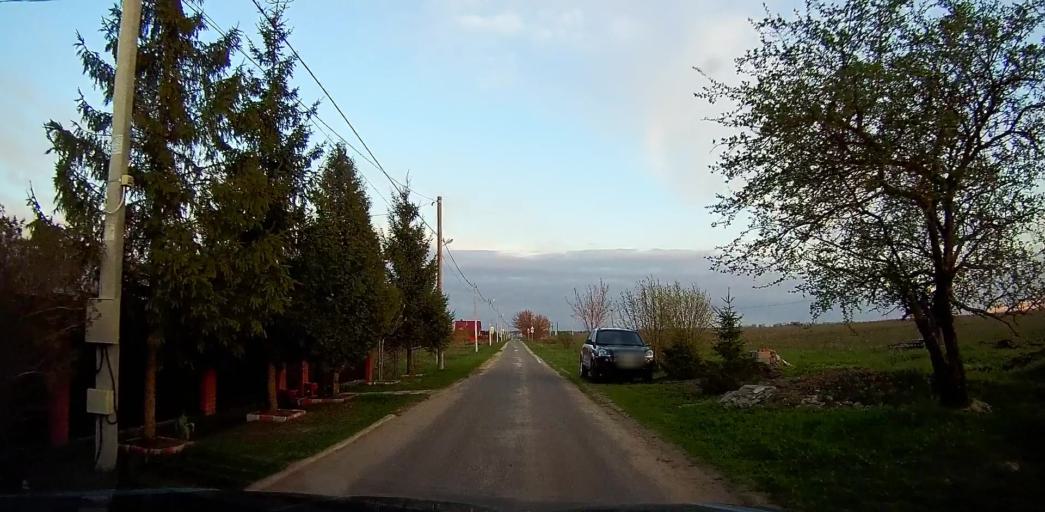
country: RU
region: Moskovskaya
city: Peski
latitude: 55.2308
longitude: 38.7329
